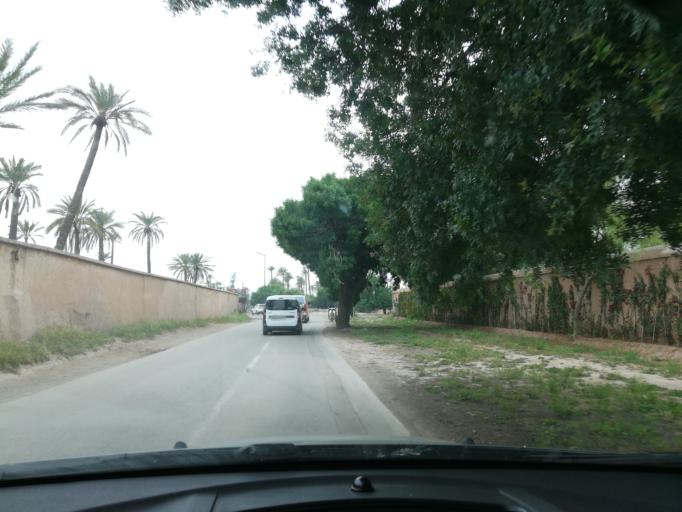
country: MA
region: Marrakech-Tensift-Al Haouz
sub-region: Marrakech
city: Marrakesh
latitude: 31.6647
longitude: -7.9675
